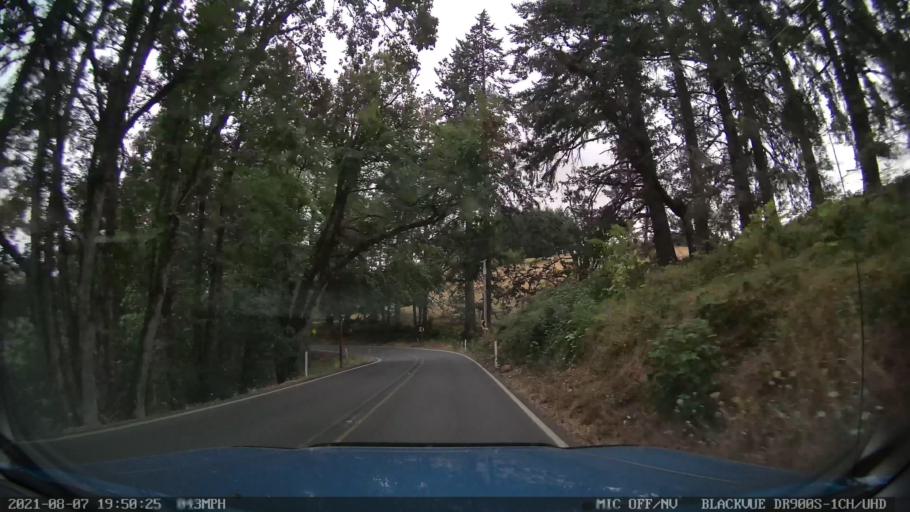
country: US
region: Oregon
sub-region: Marion County
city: Silverton
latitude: 44.9859
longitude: -122.7385
